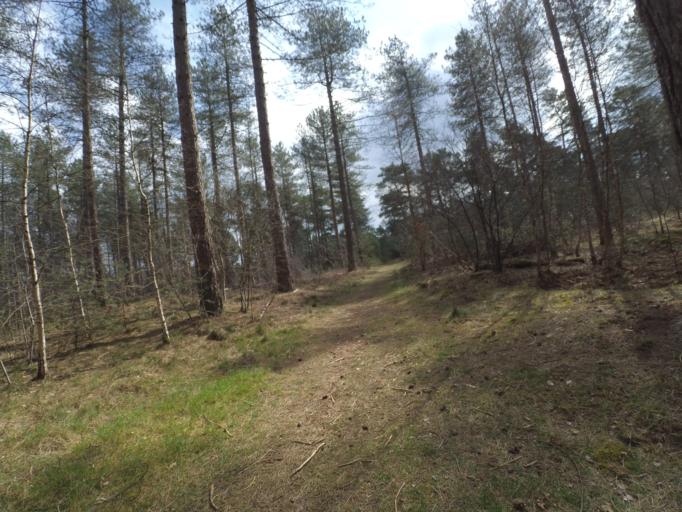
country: NL
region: Utrecht
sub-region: Gemeente Amersfoort
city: Amersfoort
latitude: 52.1257
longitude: 5.3725
